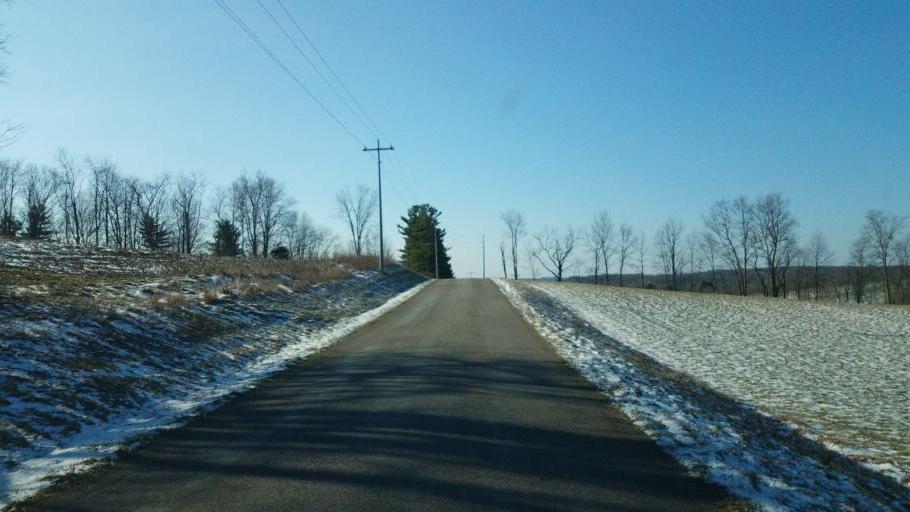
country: US
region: Ohio
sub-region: Sandusky County
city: Bellville
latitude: 40.5741
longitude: -82.4844
